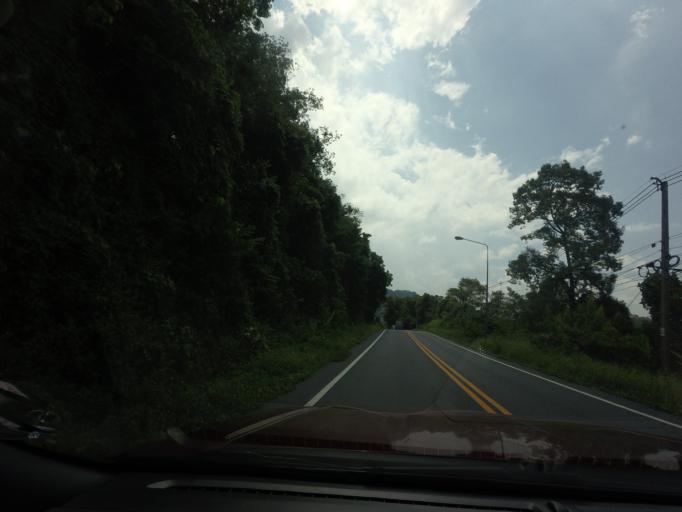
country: TH
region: Yala
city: Than To
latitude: 6.0386
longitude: 101.2102
